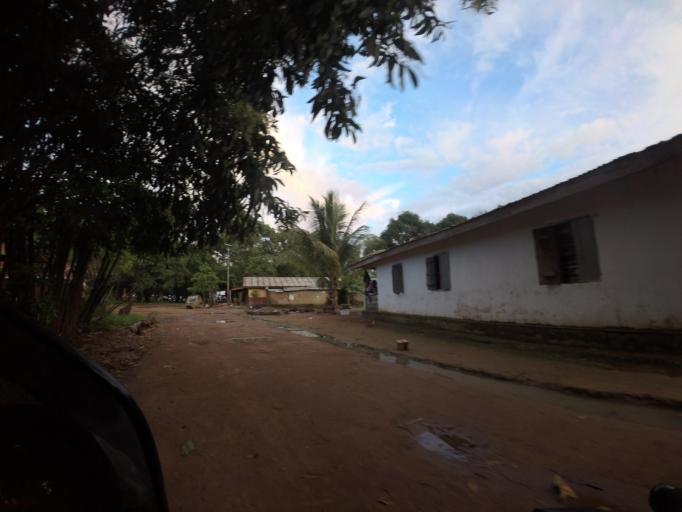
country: SL
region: Northern Province
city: Kambia
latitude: 9.1111
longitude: -12.9248
